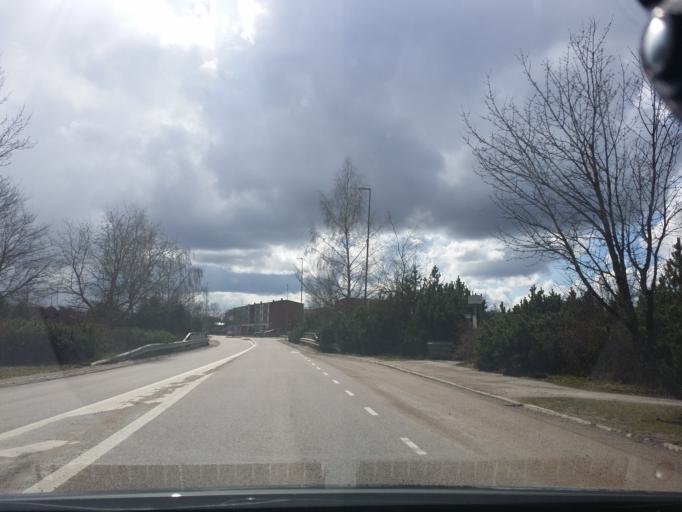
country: SE
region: Vaestmanland
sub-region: Sala Kommun
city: Sala
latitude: 59.9274
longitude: 16.5905
